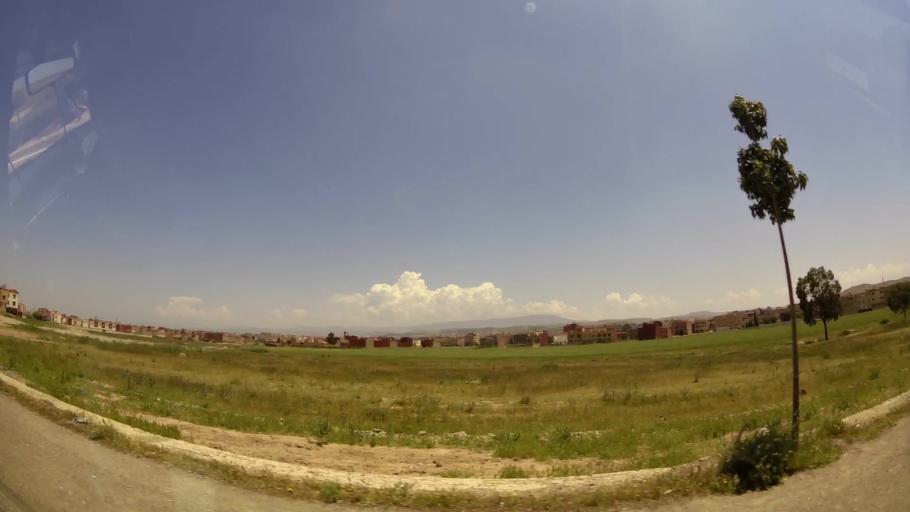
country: MA
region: Oriental
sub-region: Oujda-Angad
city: Oujda
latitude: 34.6673
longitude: -1.9505
